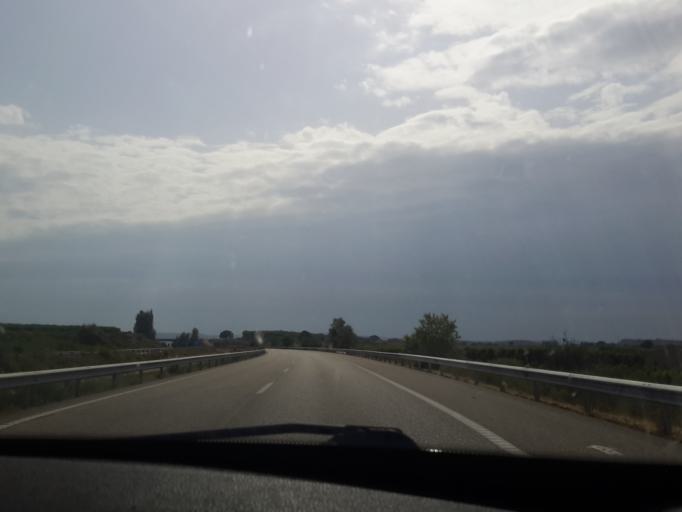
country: ES
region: Catalonia
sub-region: Provincia de Lleida
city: Seros
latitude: 41.5080
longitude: 0.4191
